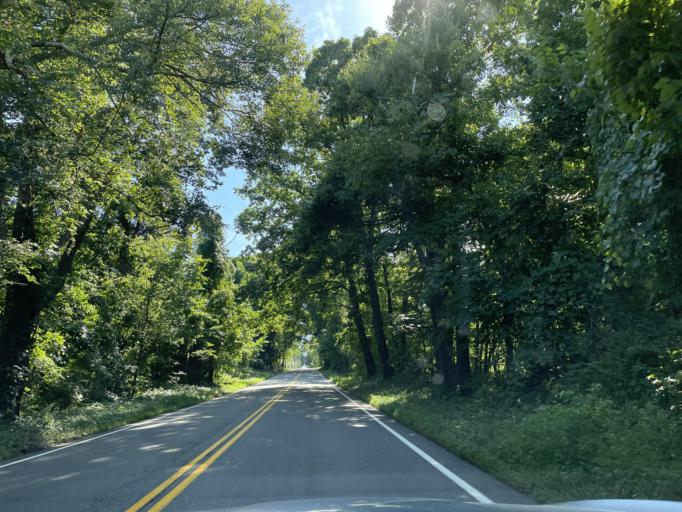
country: US
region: Massachusetts
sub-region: Worcester County
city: Sutton
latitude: 42.1431
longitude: -71.7358
